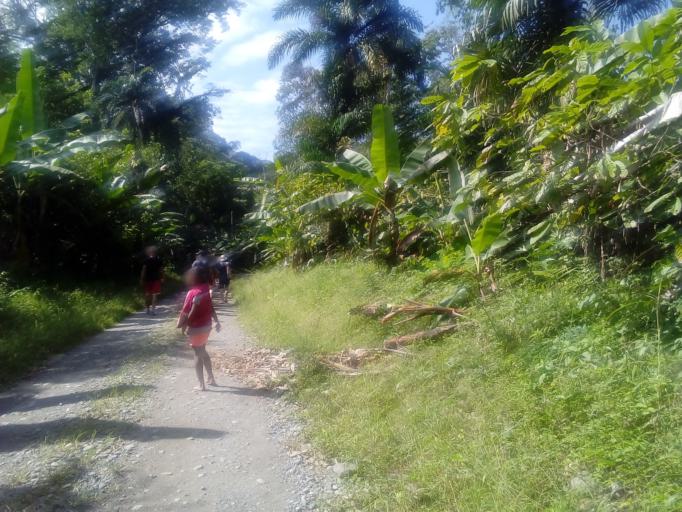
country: PA
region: Bocas del Toro
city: Barranco
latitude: 9.5101
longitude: -82.9809
